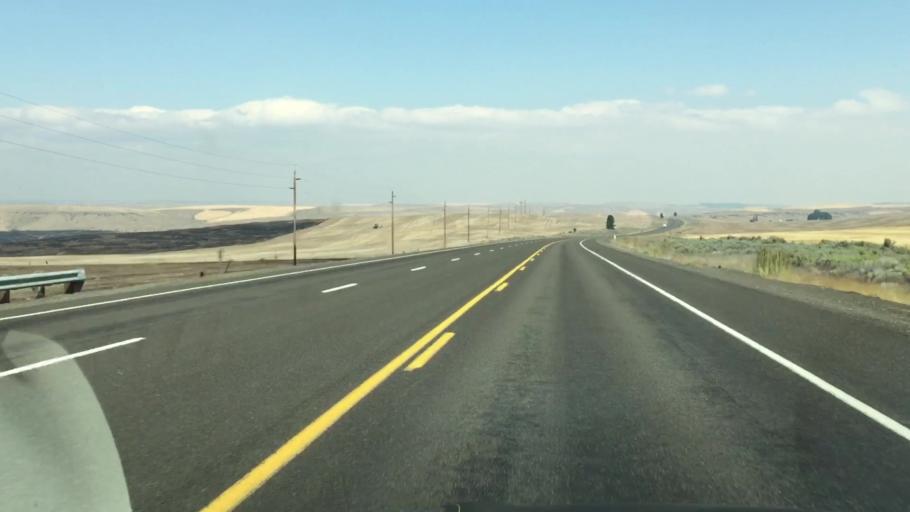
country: US
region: Oregon
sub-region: Wasco County
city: The Dalles
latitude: 45.3915
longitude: -121.1421
